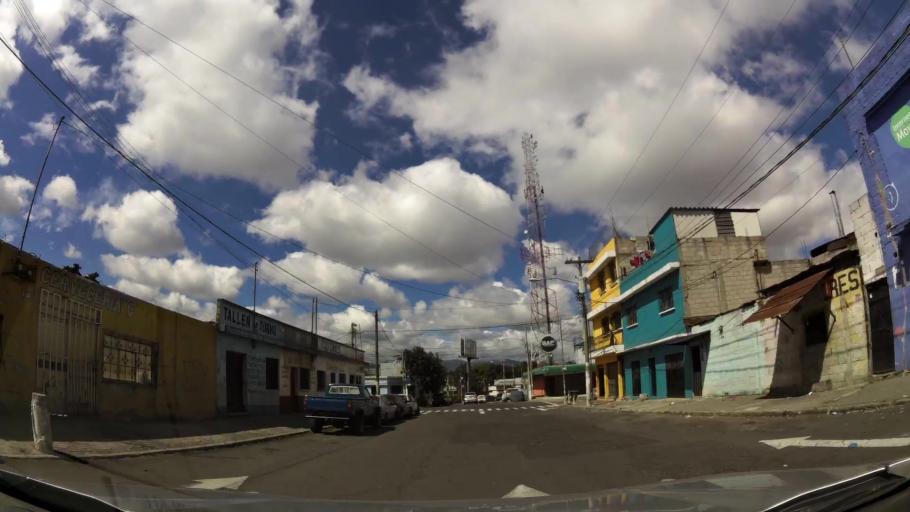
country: GT
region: Guatemala
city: Guatemala City
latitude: 14.6021
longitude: -90.5466
